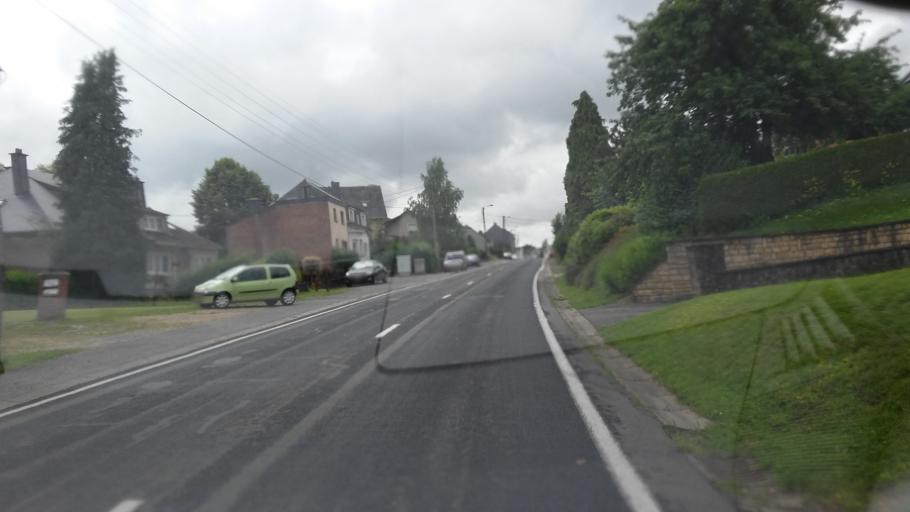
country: BE
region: Wallonia
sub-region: Province du Luxembourg
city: Arlon
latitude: 49.6897
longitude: 5.8356
